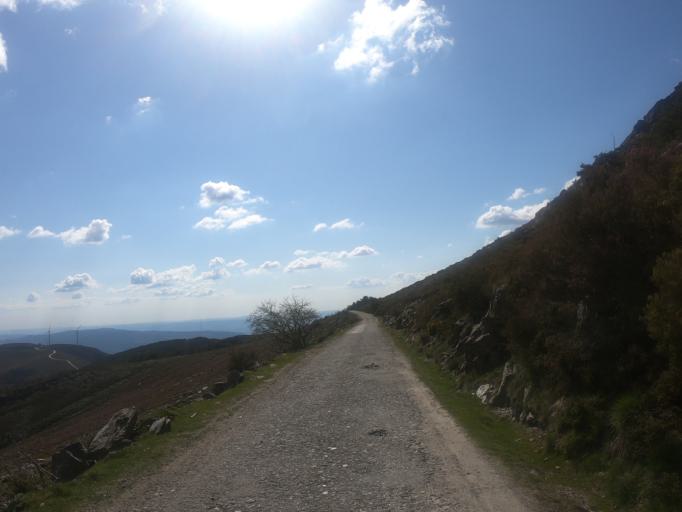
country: PT
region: Vila Real
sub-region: Mesao Frio
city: Mesao Frio
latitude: 41.2466
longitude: -7.8852
